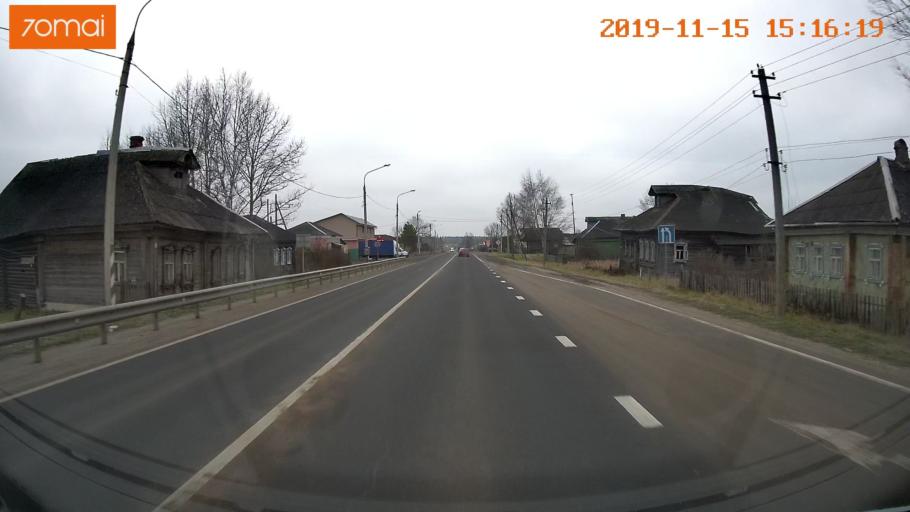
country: RU
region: Jaroslavl
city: Danilov
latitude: 58.2739
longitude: 40.1920
